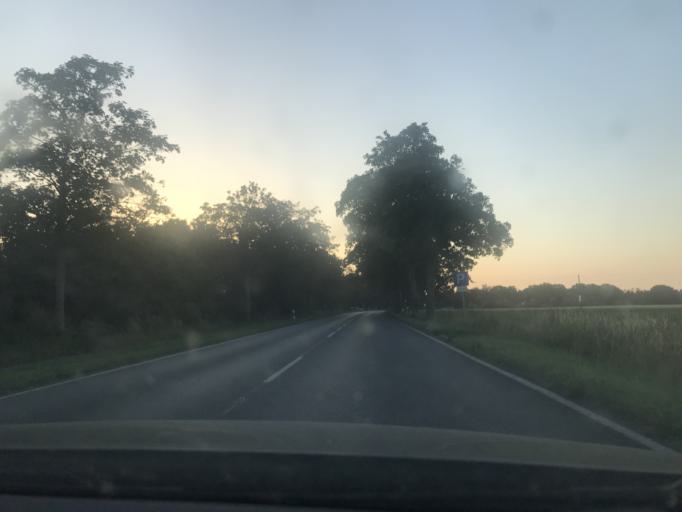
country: DE
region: North Rhine-Westphalia
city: Rheinberg
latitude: 51.5197
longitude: 6.6044
